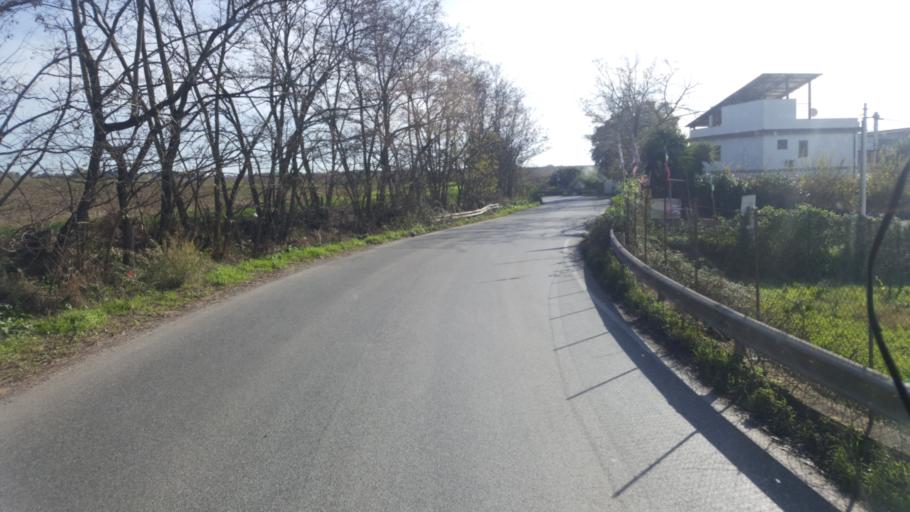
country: IT
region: Latium
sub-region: Citta metropolitana di Roma Capitale
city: Mantiglia di Ardea
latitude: 41.6900
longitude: 12.6001
